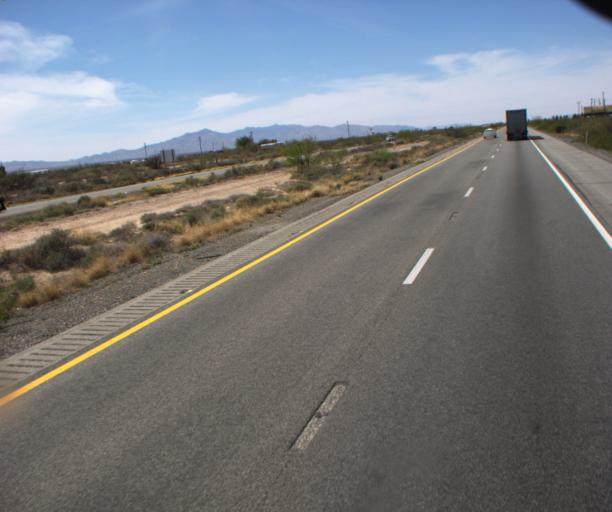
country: US
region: New Mexico
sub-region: Hidalgo County
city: Lordsburg
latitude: 32.2608
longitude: -109.2164
